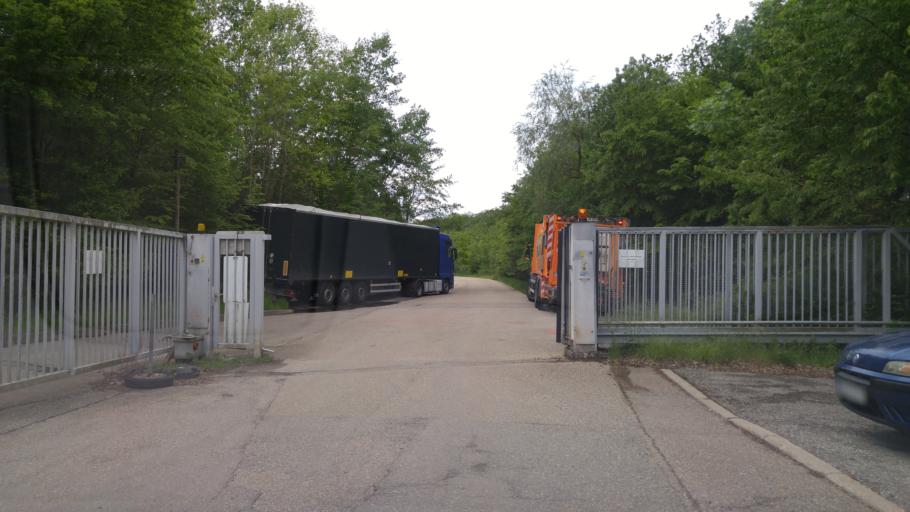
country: DE
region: Baden-Wuerttemberg
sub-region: Regierungsbezirk Stuttgart
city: Renningen
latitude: 48.7792
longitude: 8.9780
